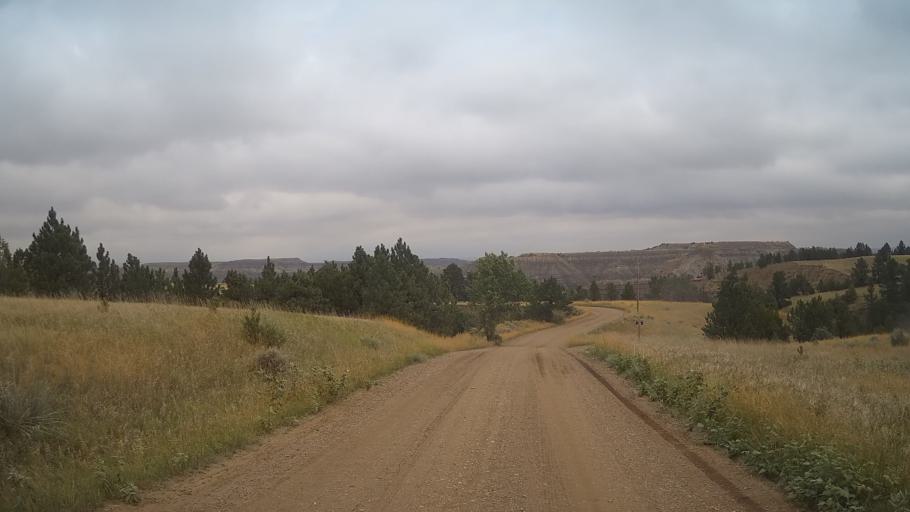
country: US
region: Montana
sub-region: Dawson County
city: Glendive
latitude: 47.0585
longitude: -104.6814
